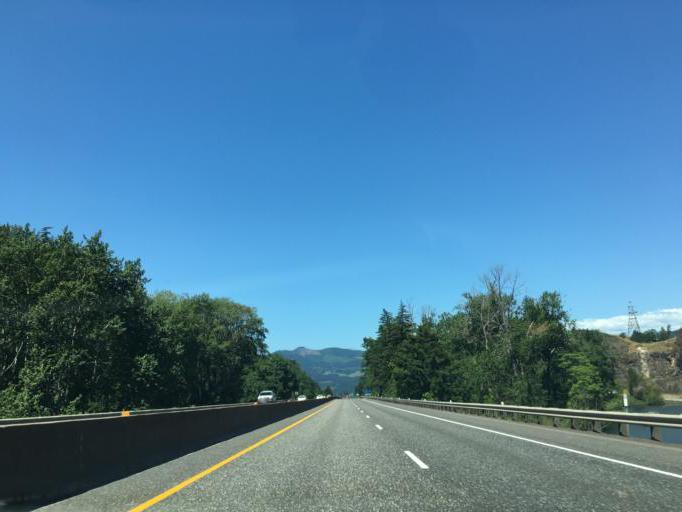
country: US
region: Washington
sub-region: Klickitat County
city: White Salmon
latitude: 45.7006
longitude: -121.4717
